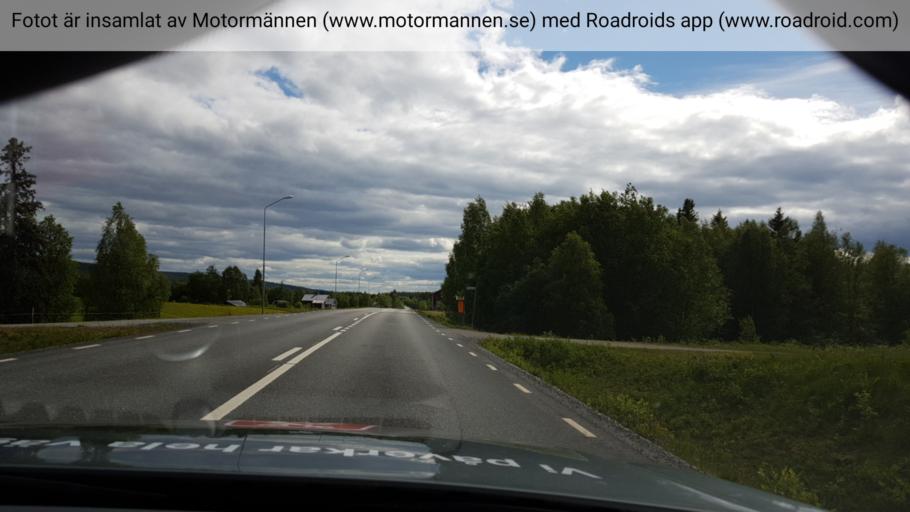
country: SE
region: Jaemtland
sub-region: Stroemsunds Kommun
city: Stroemsund
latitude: 64.0593
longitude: 15.5511
